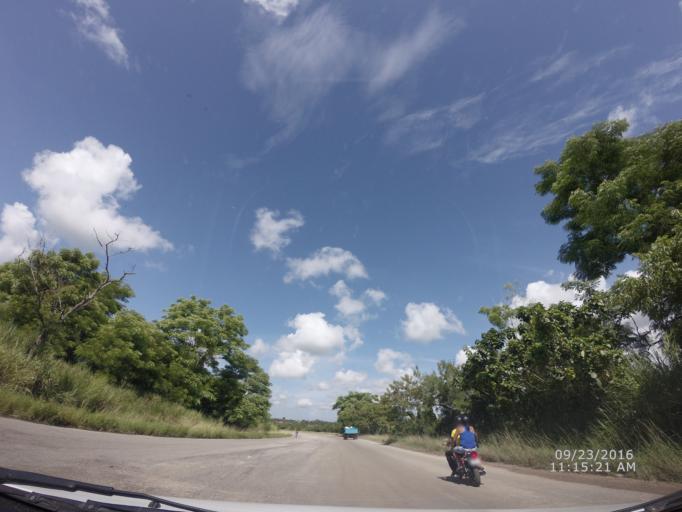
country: CU
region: La Habana
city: Arroyo Naranjo
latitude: 23.0392
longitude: -82.3103
